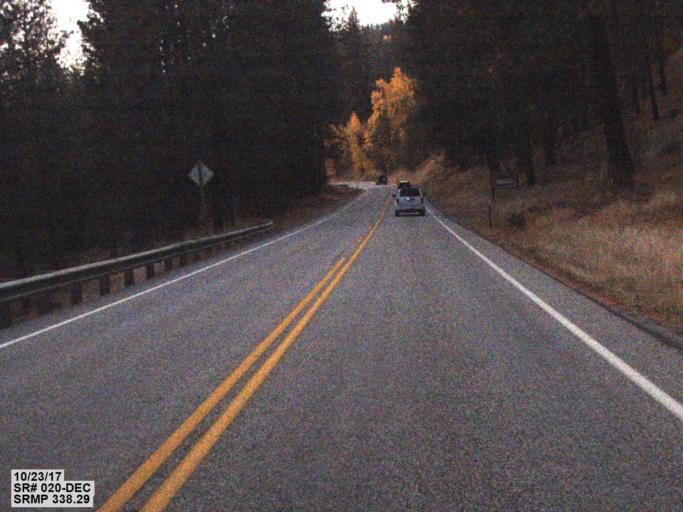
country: US
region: Washington
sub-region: Stevens County
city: Kettle Falls
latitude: 48.5909
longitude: -118.1615
